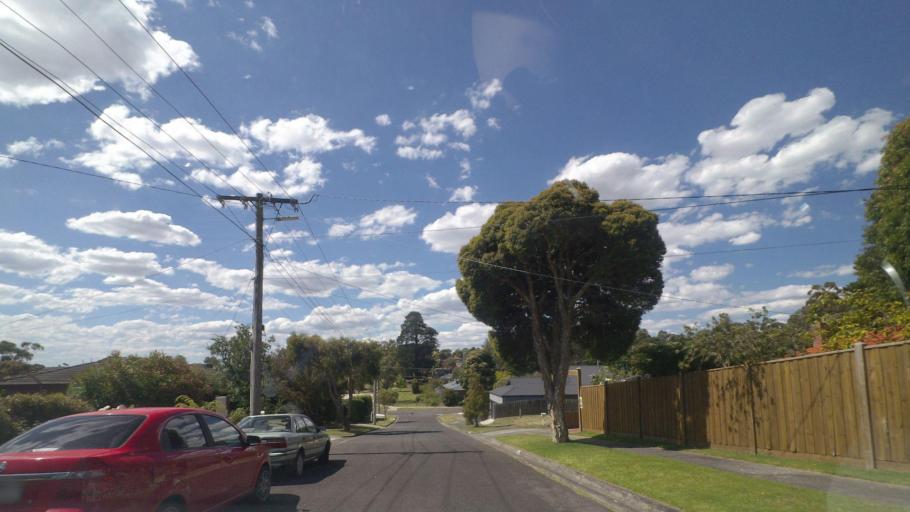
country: AU
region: Victoria
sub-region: Yarra Ranges
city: Kilsyth
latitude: -37.8044
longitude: 145.3275
